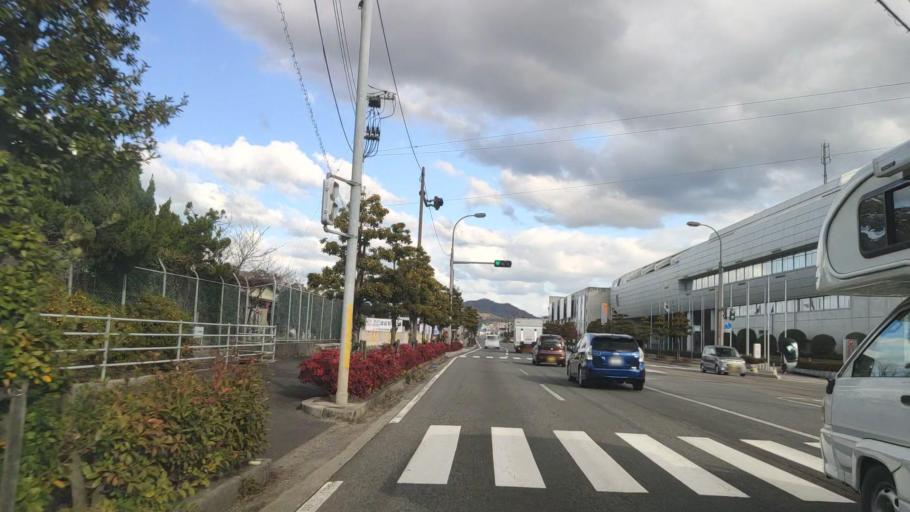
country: JP
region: Ehime
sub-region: Shikoku-chuo Shi
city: Matsuyama
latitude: 33.8491
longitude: 132.7133
